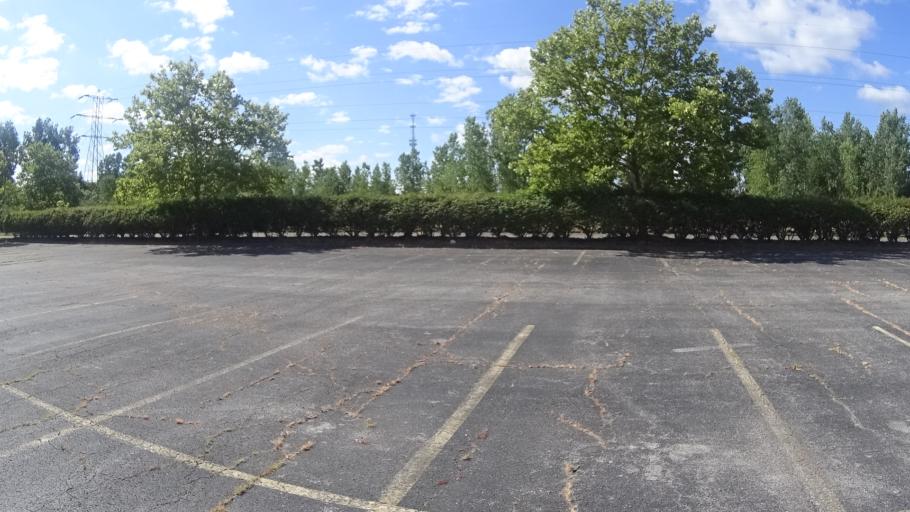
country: US
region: Ohio
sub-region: Erie County
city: Sandusky
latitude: 41.4033
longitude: -82.6535
